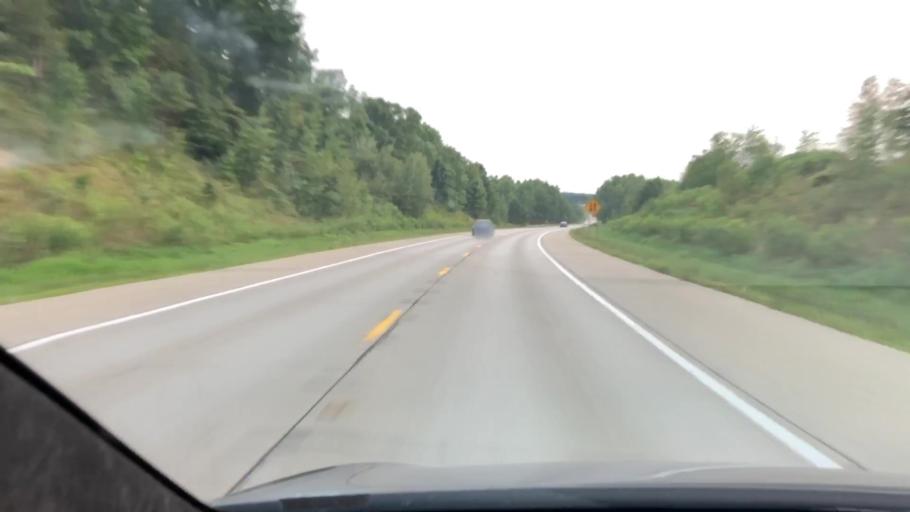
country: US
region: Pennsylvania
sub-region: Mercer County
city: Grove City
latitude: 41.2246
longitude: -79.9608
